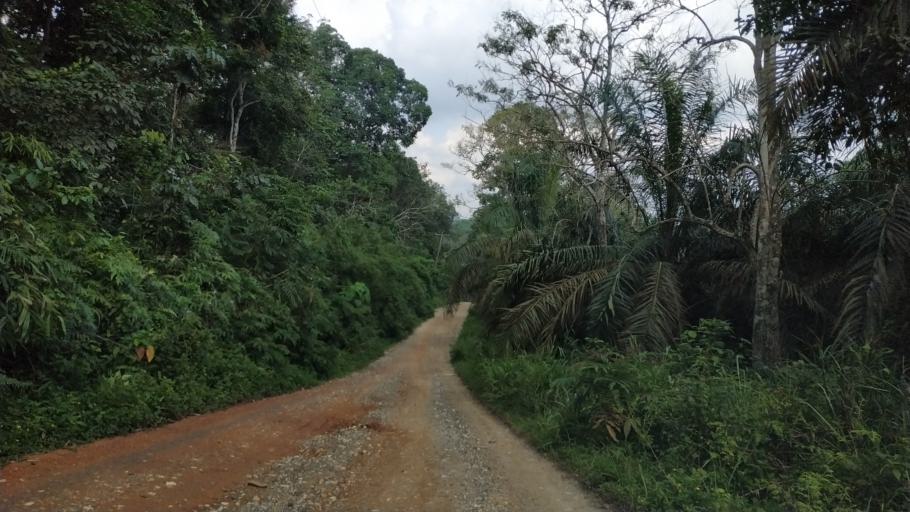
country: ID
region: Riau
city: Pangkalan Kasai
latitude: -0.7267
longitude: 102.4755
